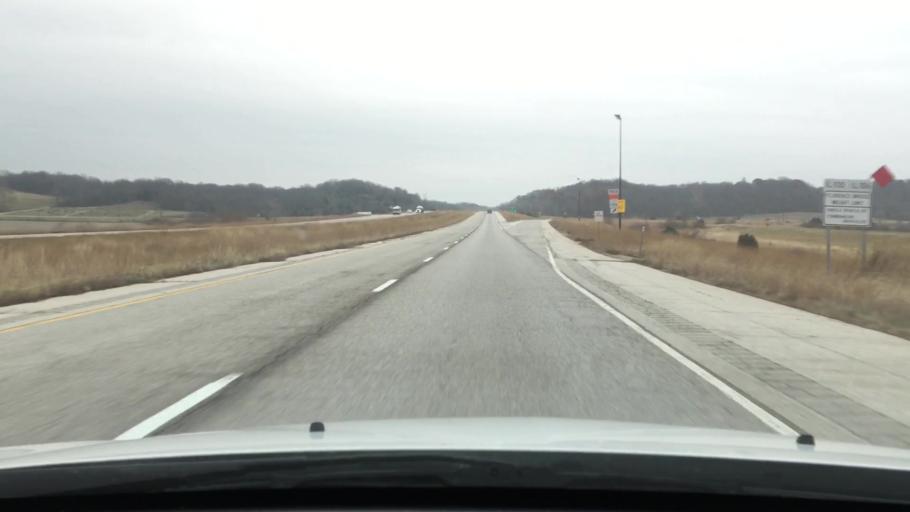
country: US
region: Illinois
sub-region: Scott County
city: Winchester
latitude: 39.6850
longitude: -90.5790
